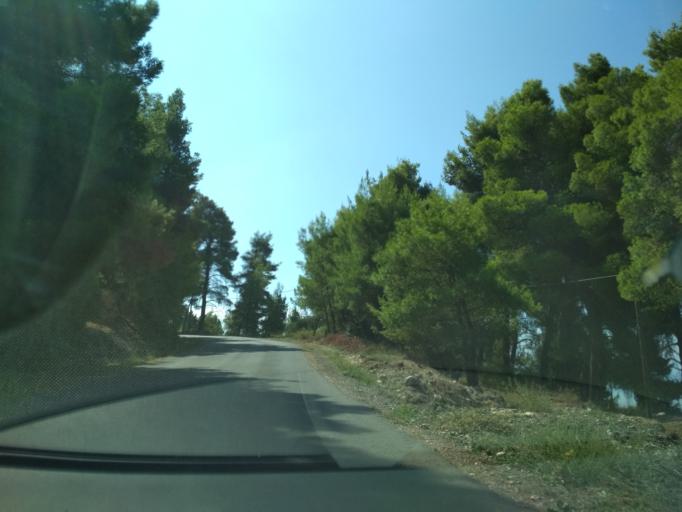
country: GR
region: Central Greece
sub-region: Nomos Evvoias
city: Roviai
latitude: 38.8164
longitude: 23.2738
